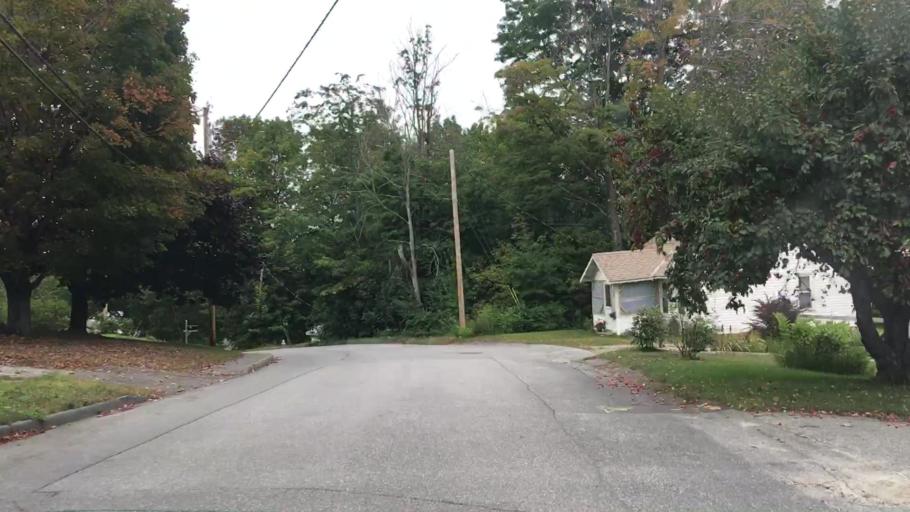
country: US
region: Maine
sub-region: Kennebec County
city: Hallowell
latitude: 44.2708
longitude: -69.7920
